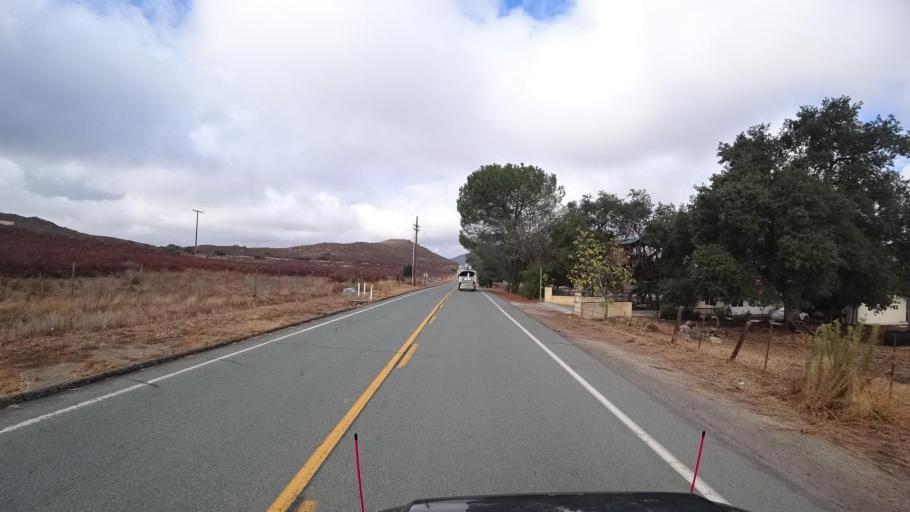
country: MX
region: Baja California
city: Tecate
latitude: 32.6153
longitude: -116.5986
